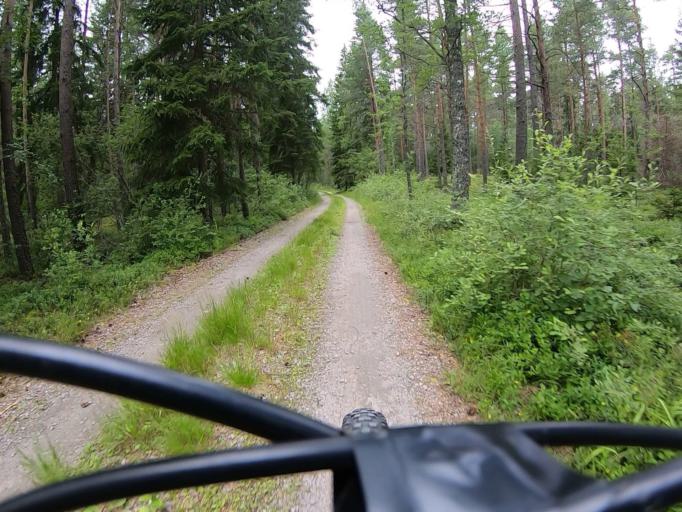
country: FI
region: Varsinais-Suomi
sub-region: Vakka-Suomi
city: Uusikaupunki
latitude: 60.8359
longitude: 21.3990
